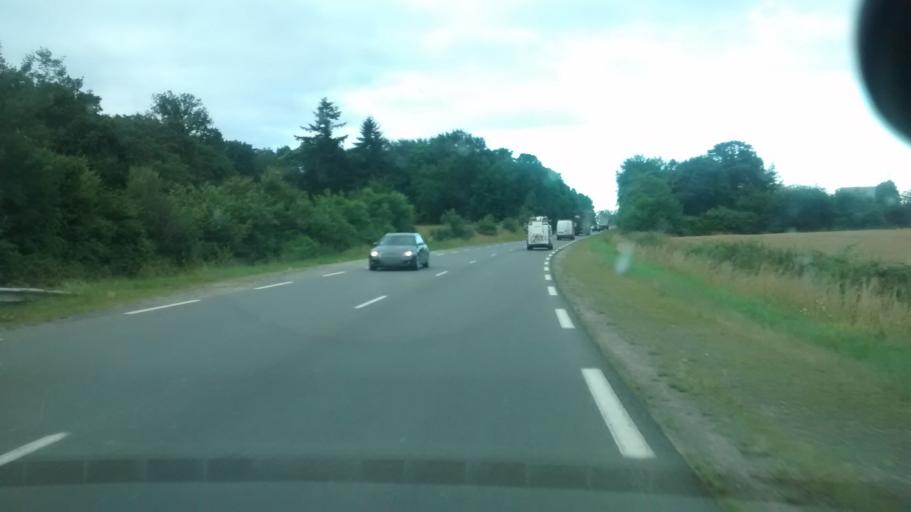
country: FR
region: Brittany
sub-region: Departement d'Ille-et-Vilaine
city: Le Rheu
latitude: 48.1078
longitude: -1.7766
